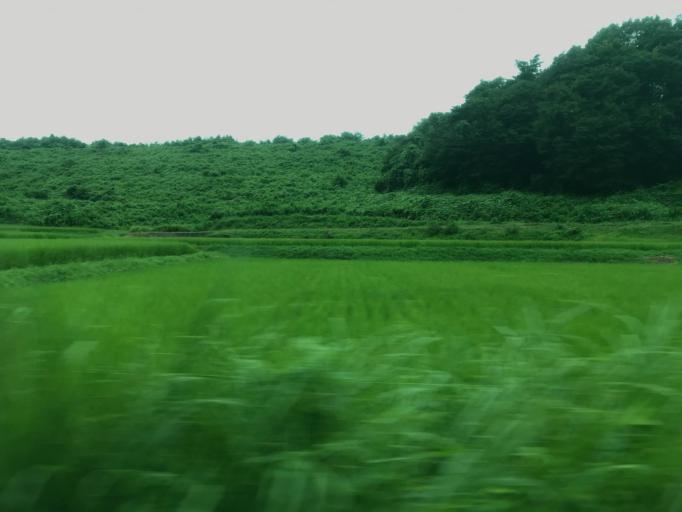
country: JP
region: Fukushima
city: Sukagawa
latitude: 37.1485
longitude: 140.2739
